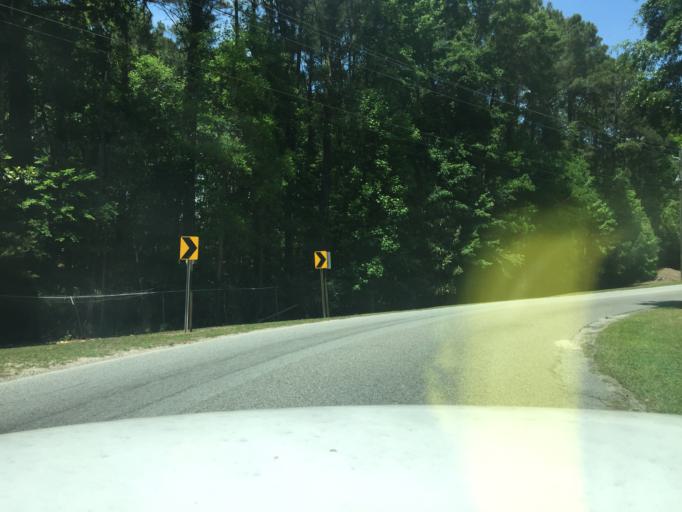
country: US
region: Georgia
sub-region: Chatham County
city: Garden City
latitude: 32.0632
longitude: -81.1667
